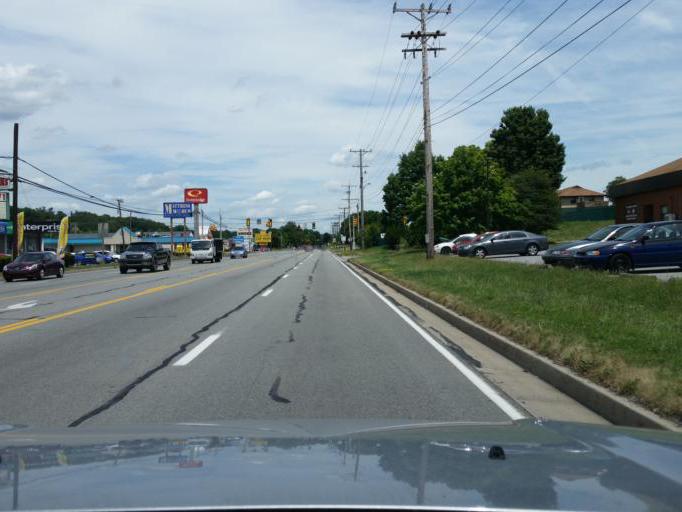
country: US
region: Pennsylvania
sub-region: Blair County
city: Lakemont
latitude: 40.4875
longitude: -78.3991
